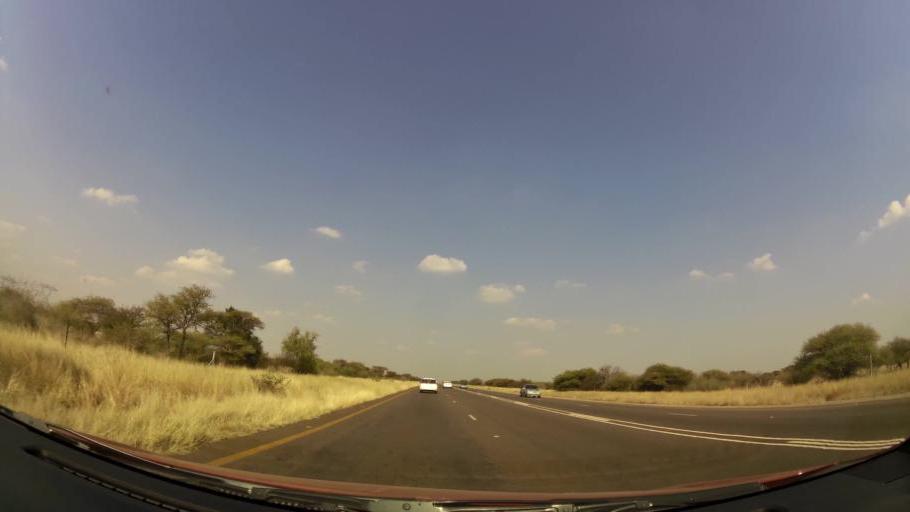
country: ZA
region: North-West
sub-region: Bojanala Platinum District Municipality
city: Mogwase
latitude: -25.3997
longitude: 27.0730
